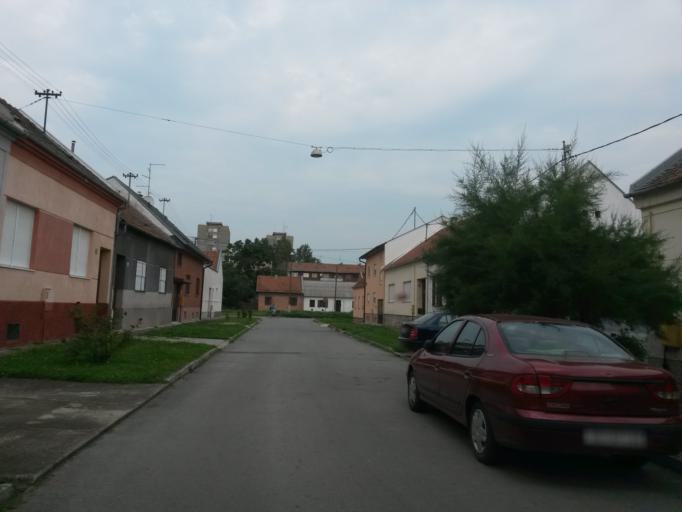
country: HR
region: Osjecko-Baranjska
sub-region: Grad Osijek
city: Osijek
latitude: 45.5523
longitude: 18.7168
